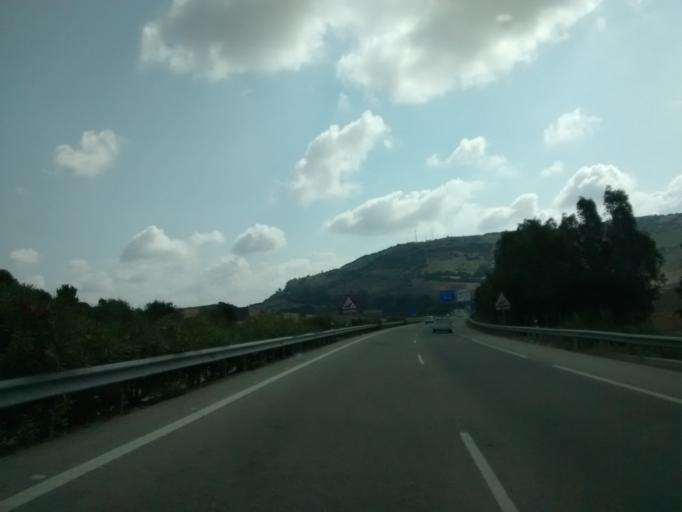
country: ES
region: Andalusia
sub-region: Provincia de Cadiz
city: Vejer de la Frontera
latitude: 36.2538
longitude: -5.9900
